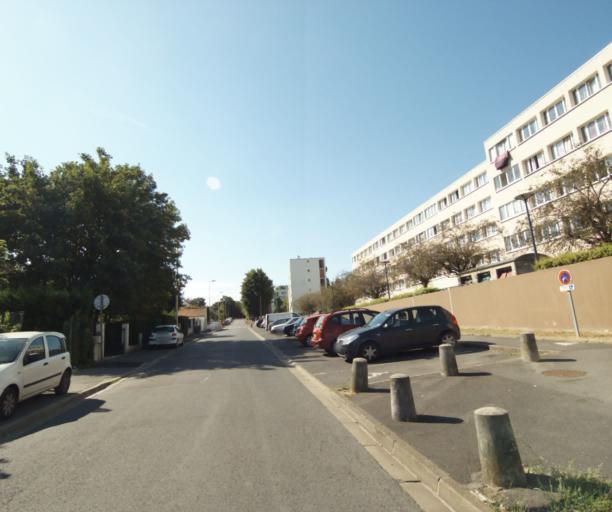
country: FR
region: Ile-de-France
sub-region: Departement de Seine-et-Marne
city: Lagny-sur-Marne
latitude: 48.8708
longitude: 2.7047
